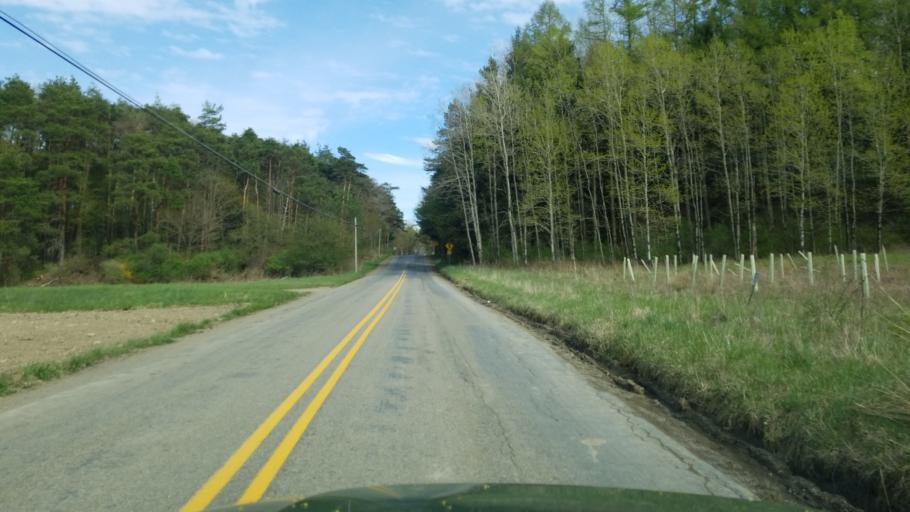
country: US
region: Pennsylvania
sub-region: Jefferson County
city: Brockway
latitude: 41.2208
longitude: -78.8428
